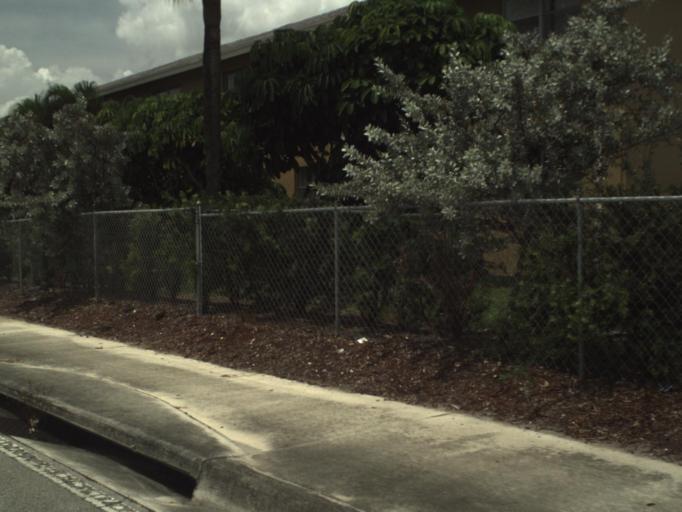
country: US
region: Florida
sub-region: Palm Beach County
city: Delray Beach
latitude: 26.4502
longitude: -80.0926
